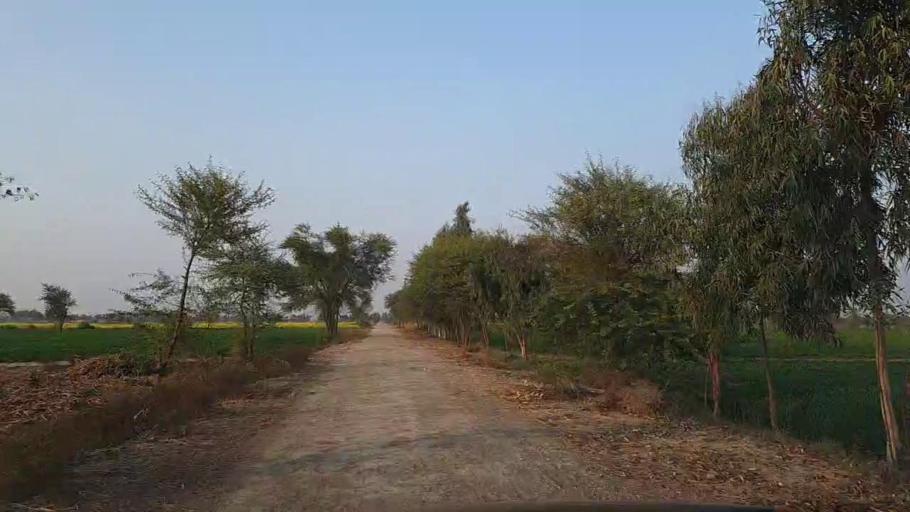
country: PK
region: Sindh
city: Daur
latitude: 26.4240
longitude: 68.3858
